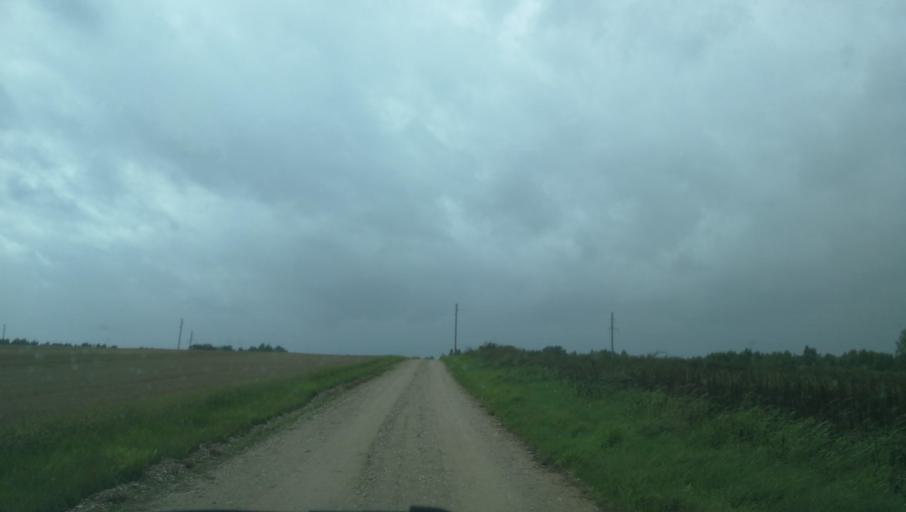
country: LV
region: Beverina
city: Murmuiza
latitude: 57.4085
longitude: 25.4596
